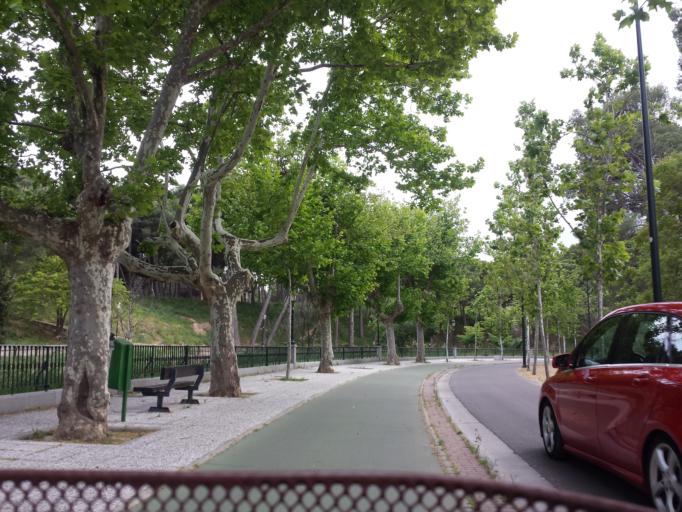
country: ES
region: Aragon
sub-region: Provincia de Zaragoza
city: Delicias
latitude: 41.6304
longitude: -0.8921
